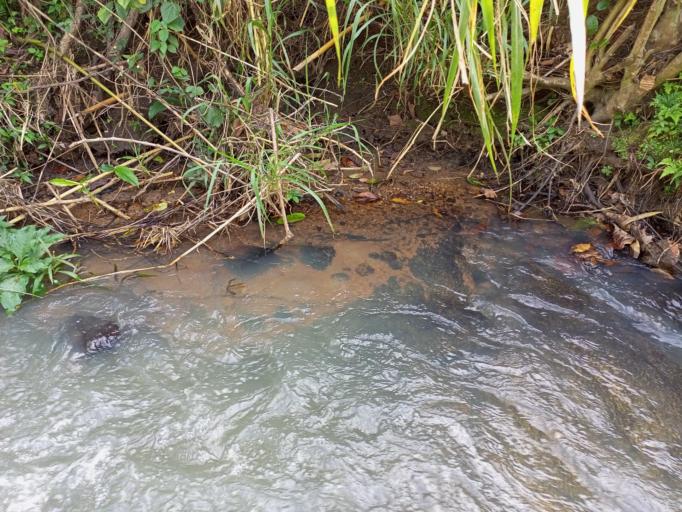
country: CD
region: Eastern Province
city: Bunia
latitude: 1.5371
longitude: 30.2956
